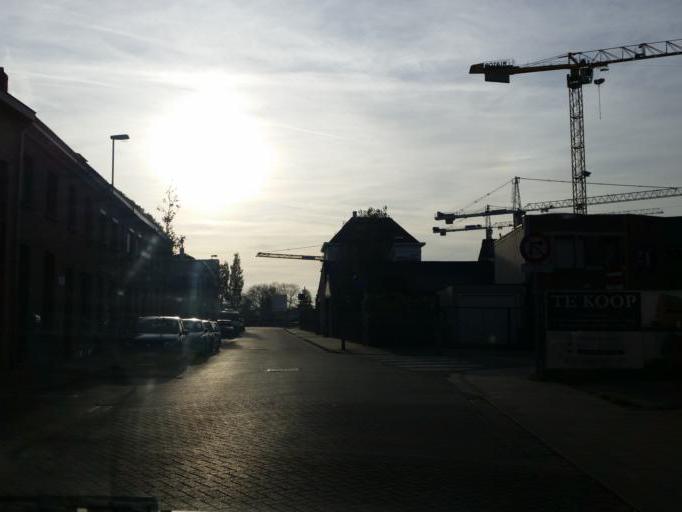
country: BE
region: Flanders
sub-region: Provincie Antwerpen
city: Hoboken
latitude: 51.1810
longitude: 4.3504
